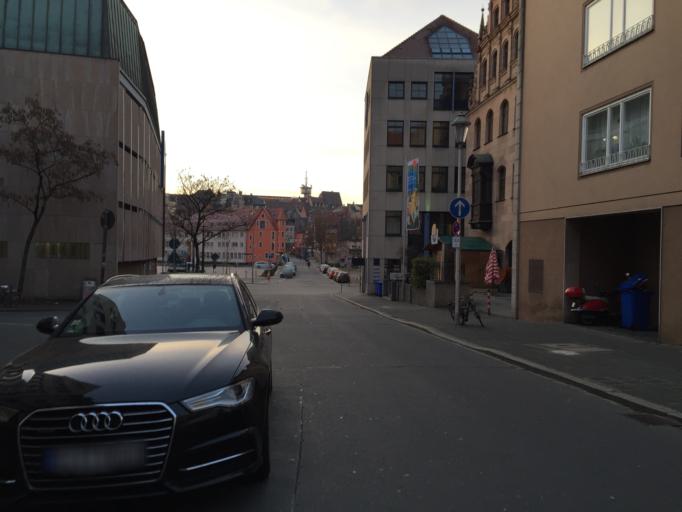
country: DE
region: Bavaria
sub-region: Regierungsbezirk Mittelfranken
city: Nuernberg
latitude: 49.4549
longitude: 11.0745
